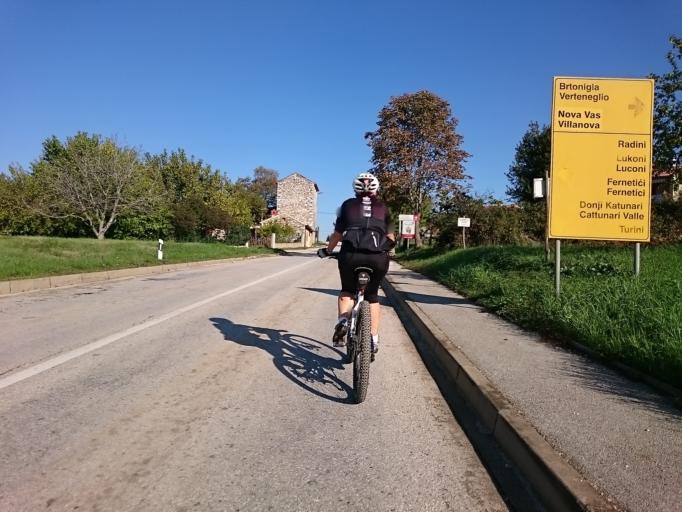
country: HR
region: Istarska
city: Buje
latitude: 45.3769
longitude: 13.6221
